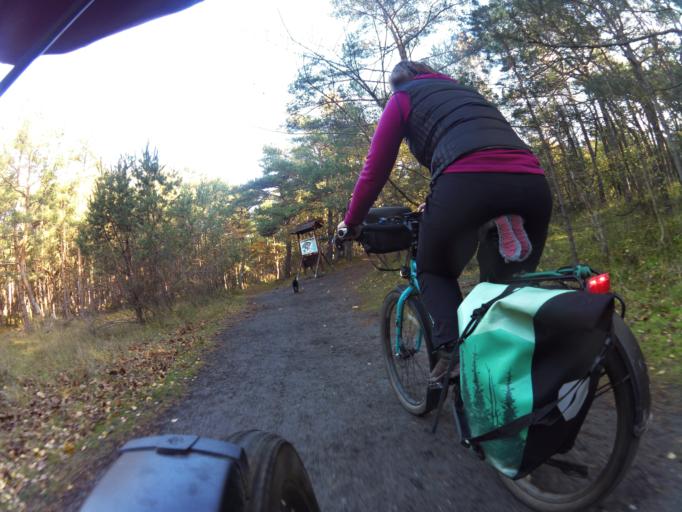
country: PL
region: Pomeranian Voivodeship
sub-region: Powiat pucki
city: Hel
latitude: 54.5965
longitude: 18.8119
